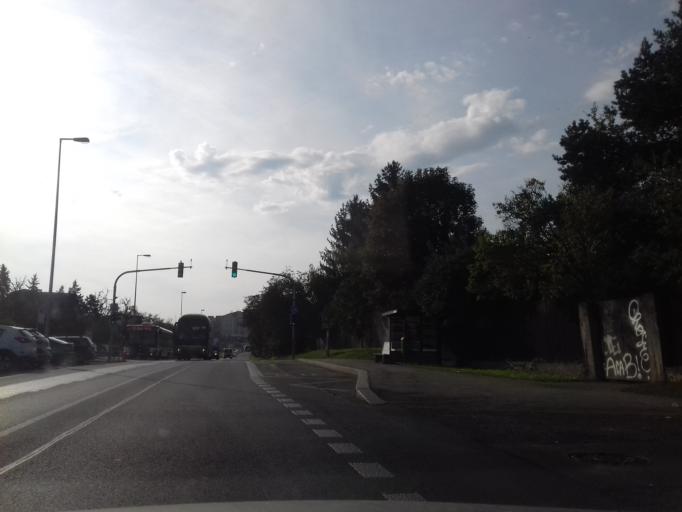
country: CZ
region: Praha
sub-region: Praha 4
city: Hodkovicky
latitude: 50.0248
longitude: 14.4598
